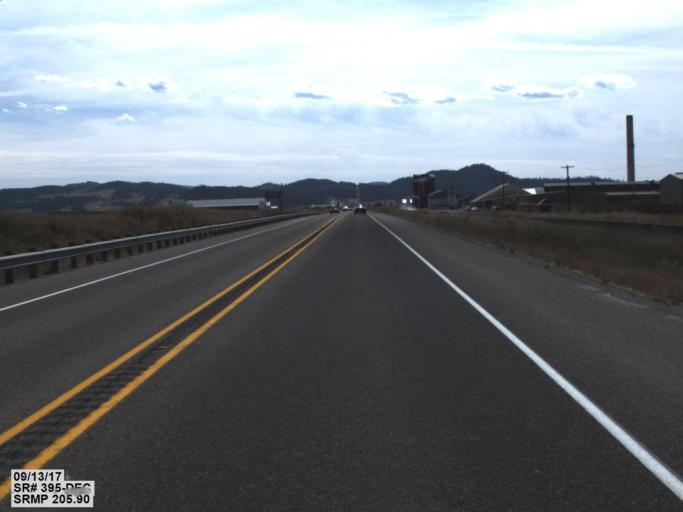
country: US
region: Washington
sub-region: Stevens County
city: Chewelah
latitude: 48.2585
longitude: -117.7154
